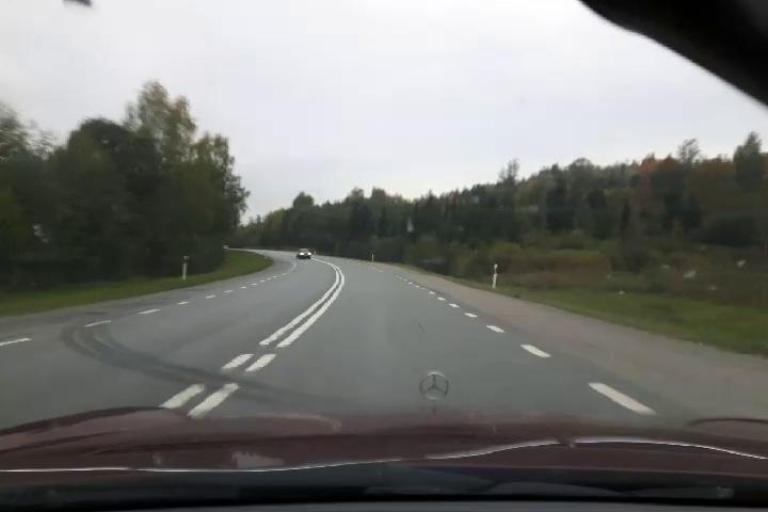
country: SE
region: Vaesternorrland
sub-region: Kramfors Kommun
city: Nordingra
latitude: 63.0055
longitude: 18.2630
